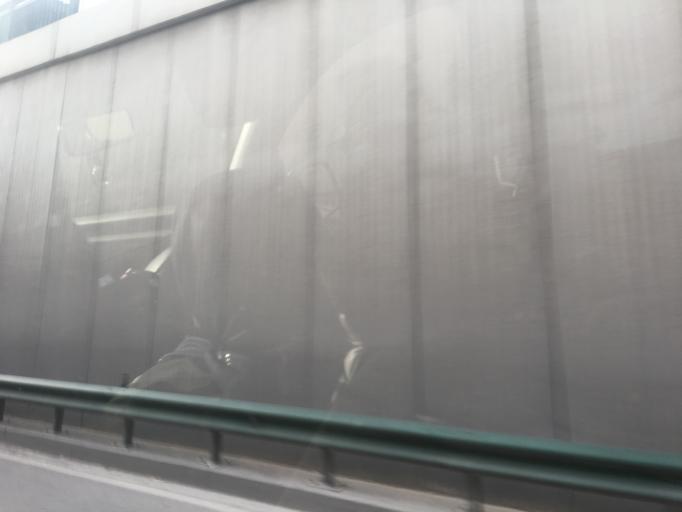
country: TR
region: Bursa
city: Yildirim
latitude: 40.2123
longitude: 28.9936
